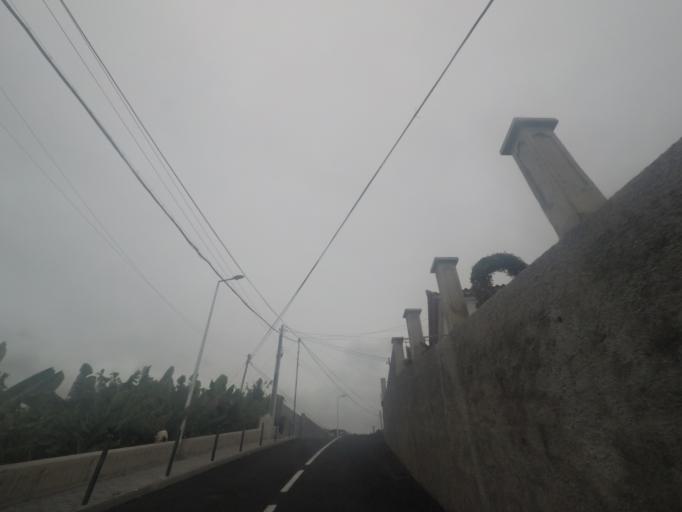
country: PT
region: Madeira
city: Camara de Lobos
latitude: 32.6624
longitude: -16.9716
